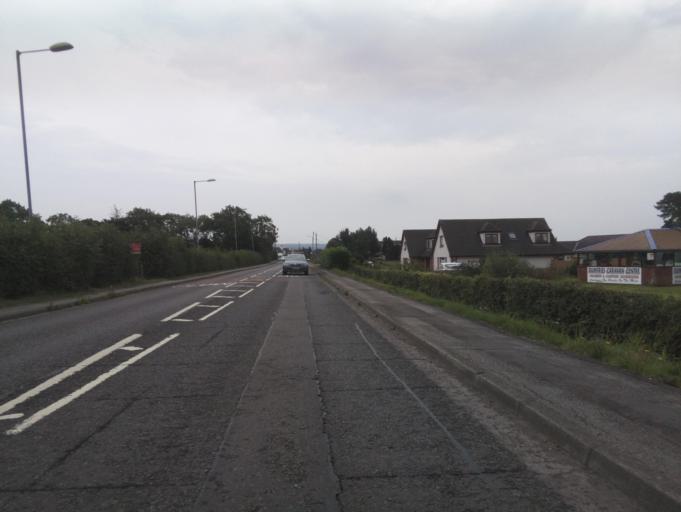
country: GB
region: Scotland
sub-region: Dumfries and Galloway
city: Locharbriggs
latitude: 55.0691
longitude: -3.5689
